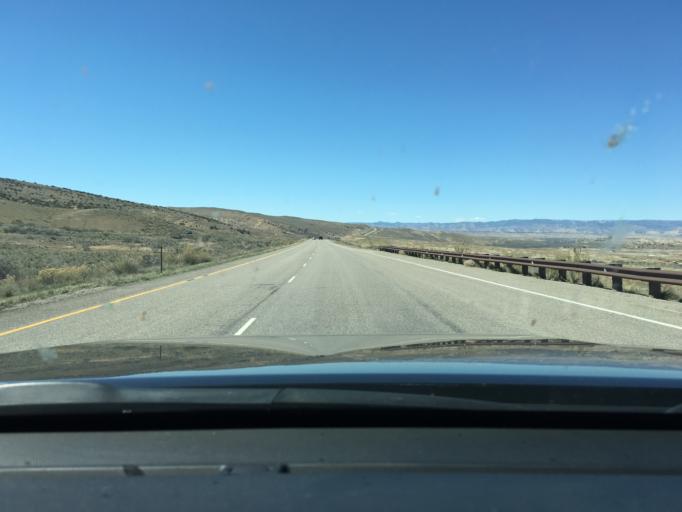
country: US
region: Colorado
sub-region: Mesa County
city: Loma
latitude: 39.2165
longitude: -108.8717
